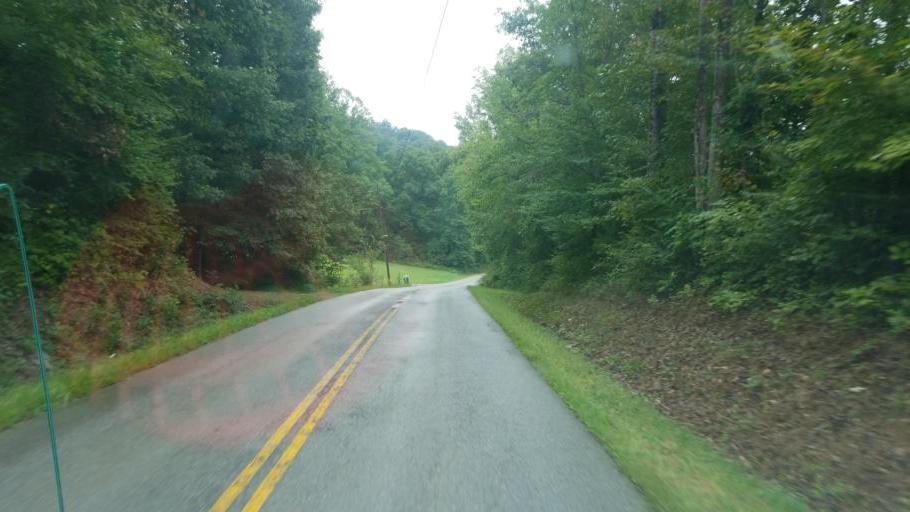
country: US
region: Kentucky
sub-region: Fleming County
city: Flemingsburg
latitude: 38.3821
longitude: -83.5419
